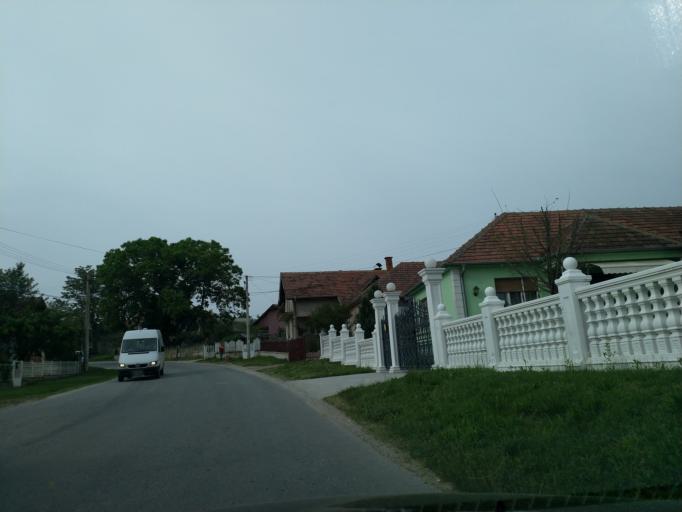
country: RS
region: Central Serbia
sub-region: Pomoravski Okrug
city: Jagodina
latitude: 43.9679
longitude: 21.2276
